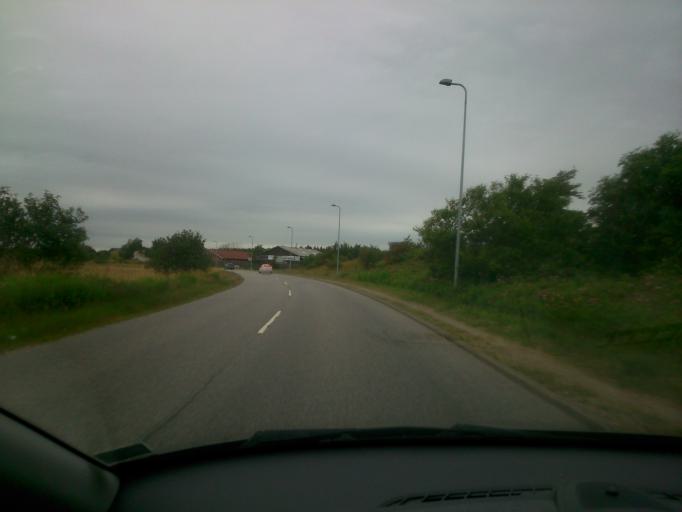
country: DK
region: Central Jutland
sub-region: Ringkobing-Skjern Kommune
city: Skjern
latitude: 55.9498
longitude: 8.4834
